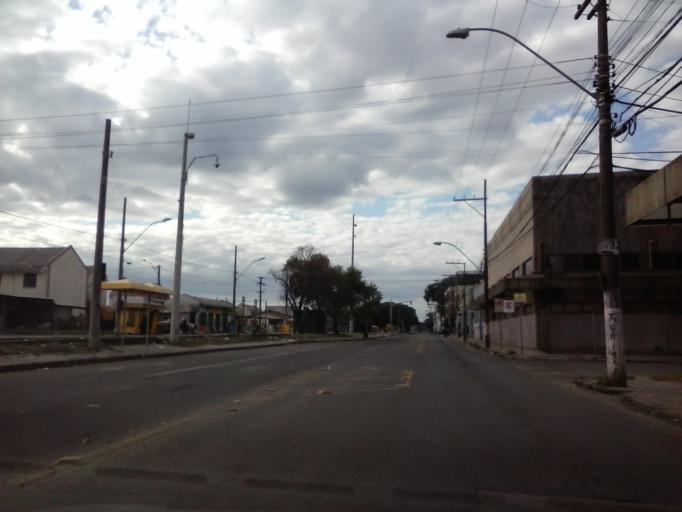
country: BR
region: Rio Grande do Sul
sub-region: Porto Alegre
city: Porto Alegre
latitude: -30.0190
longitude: -51.2139
